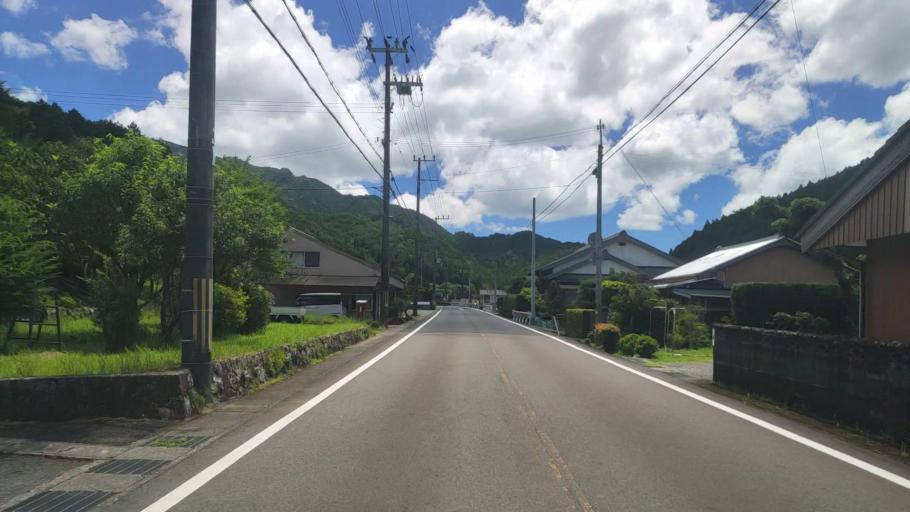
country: JP
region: Mie
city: Owase
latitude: 33.9760
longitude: 136.0550
